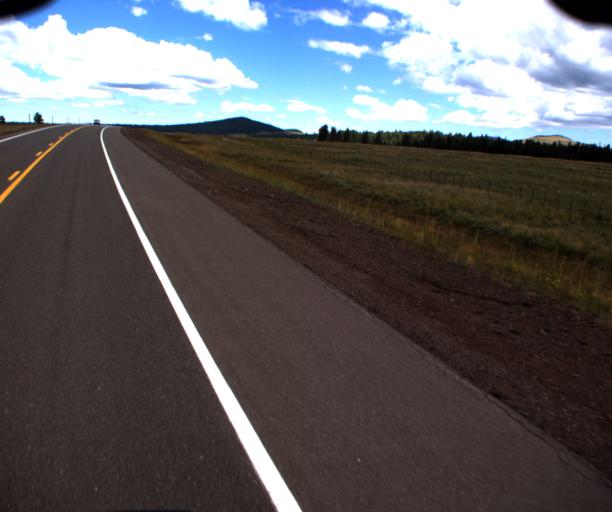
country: US
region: Arizona
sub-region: Apache County
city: Eagar
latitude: 34.0242
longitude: -109.5803
